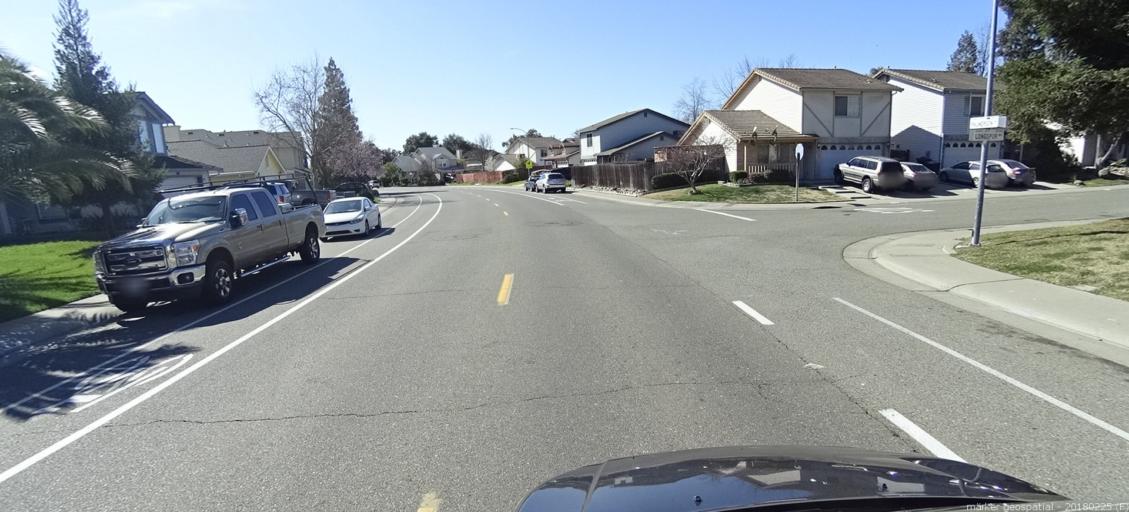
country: US
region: California
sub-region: Sacramento County
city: Antelope
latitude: 38.7237
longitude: -121.3575
